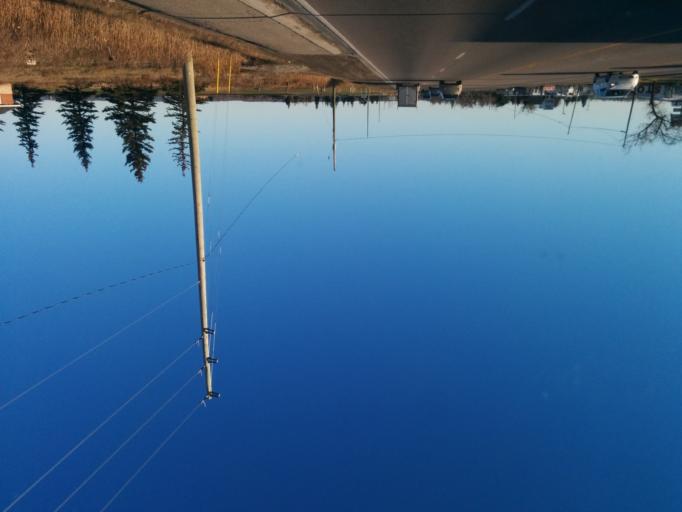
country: CA
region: Ontario
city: Brampton
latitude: 43.7739
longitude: -79.8783
